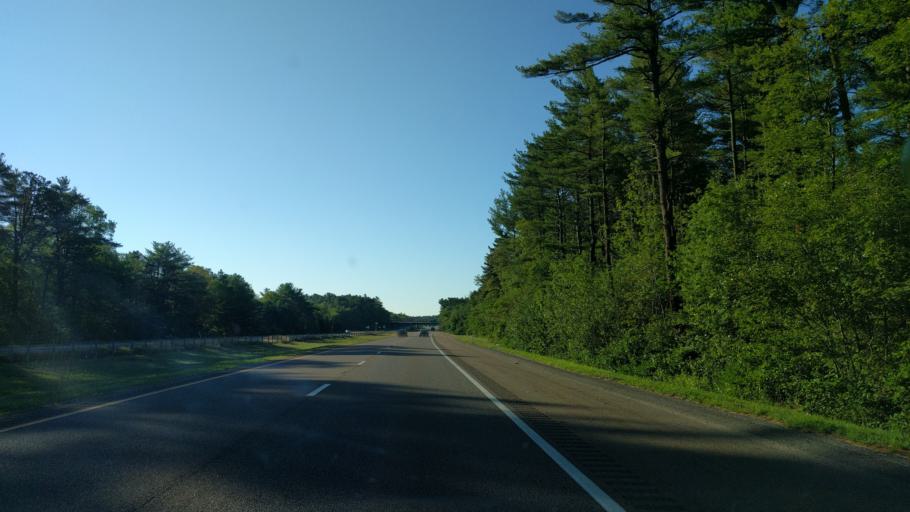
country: US
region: Massachusetts
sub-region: Plymouth County
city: Middleborough Center
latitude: 41.9065
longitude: -70.9711
